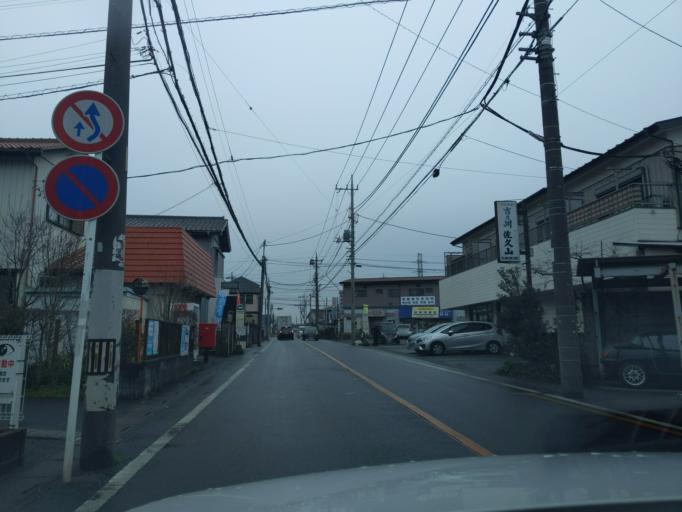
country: JP
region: Saitama
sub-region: Kawaguchi-shi
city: Hatogaya-honcho
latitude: 35.8561
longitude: 139.7231
